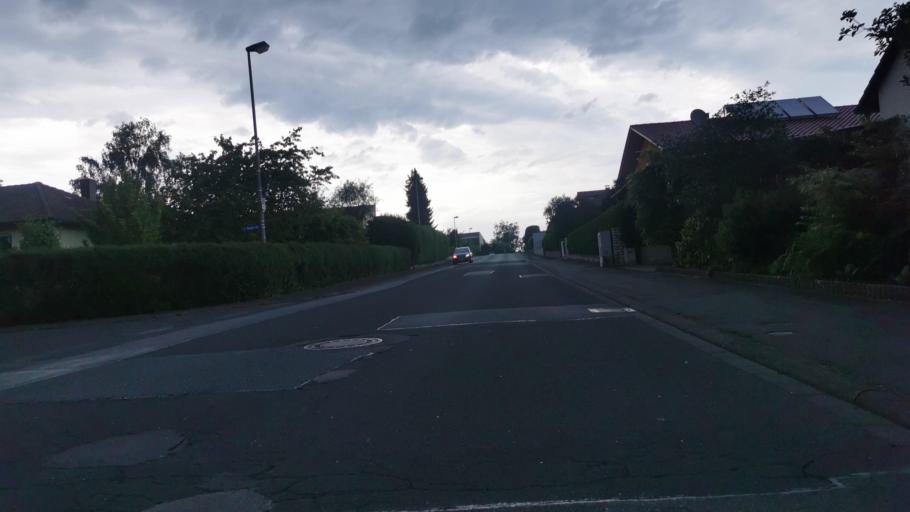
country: DE
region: Bavaria
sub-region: Regierungsbezirk Mittelfranken
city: Hochstadt an der Aisch
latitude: 49.7113
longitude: 10.8169
